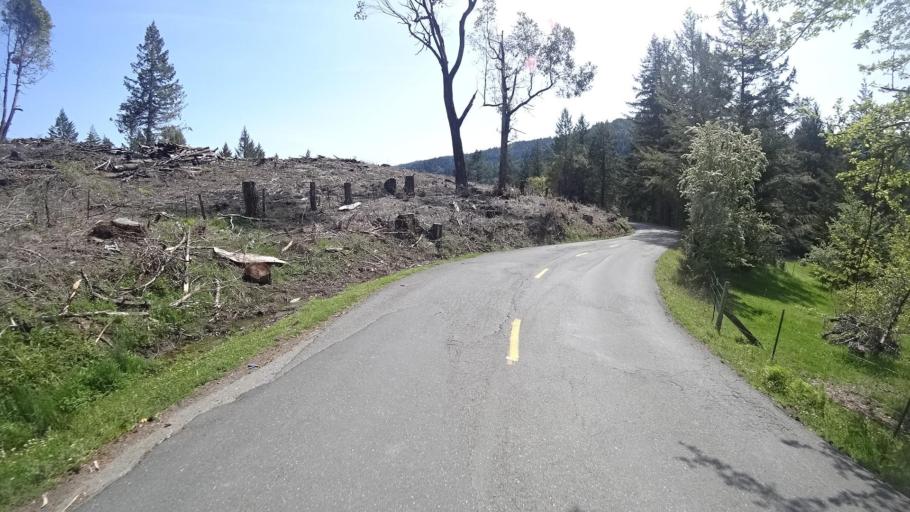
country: US
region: California
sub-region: Humboldt County
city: Redway
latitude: 40.3822
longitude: -123.7429
